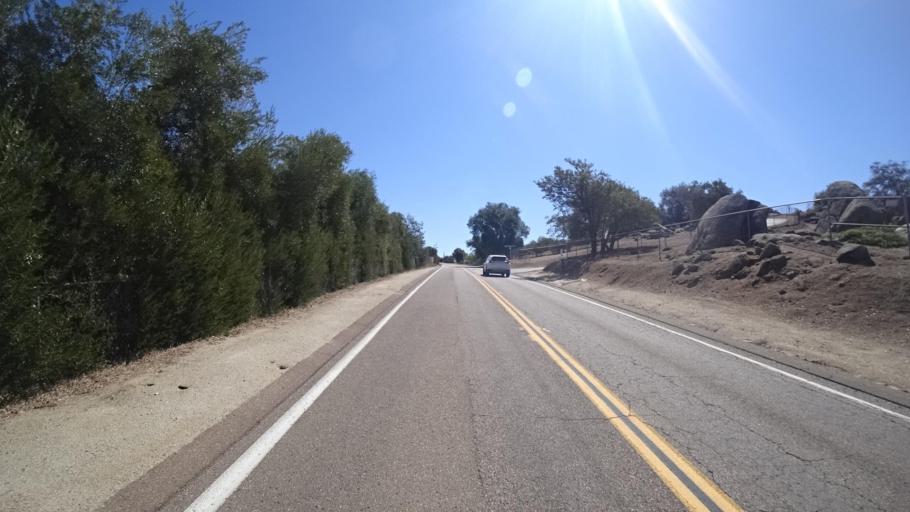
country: US
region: California
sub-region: San Diego County
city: Ramona
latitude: 33.0362
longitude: -116.8288
